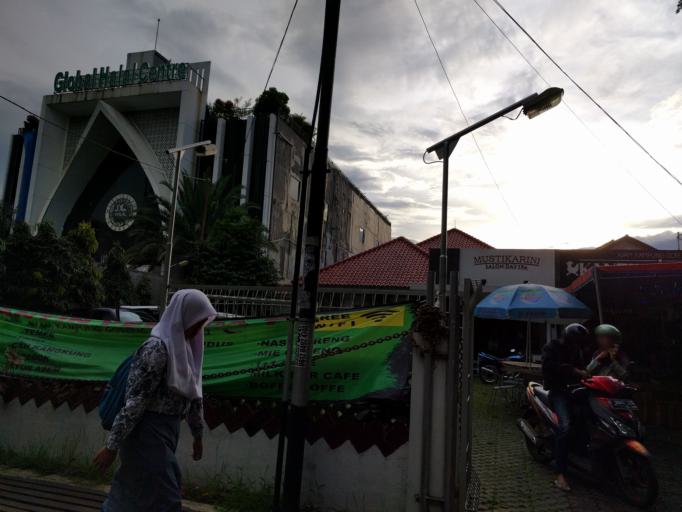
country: ID
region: West Java
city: Bogor
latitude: -6.5797
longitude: 106.7966
